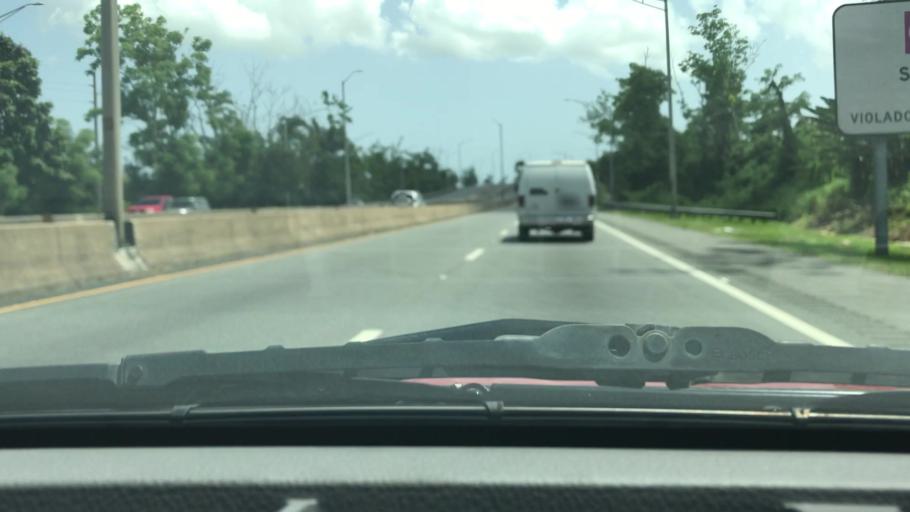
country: PR
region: Bayamon
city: Bayamon
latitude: 18.3770
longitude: -66.1621
